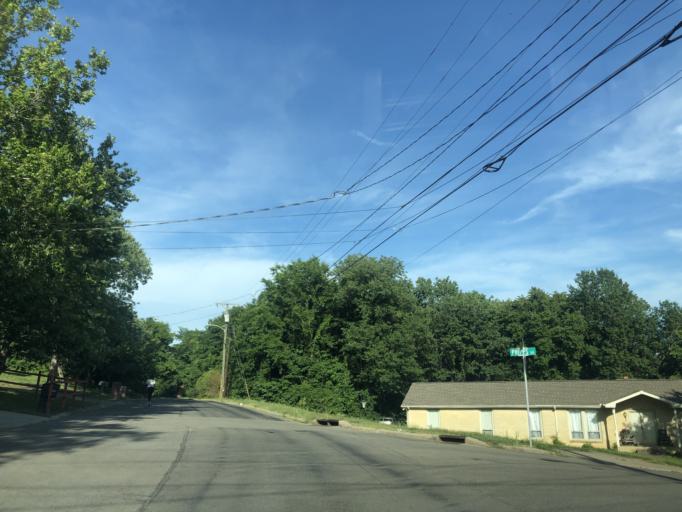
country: US
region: Tennessee
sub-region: Davidson County
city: Nashville
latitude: 36.2237
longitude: -86.8444
